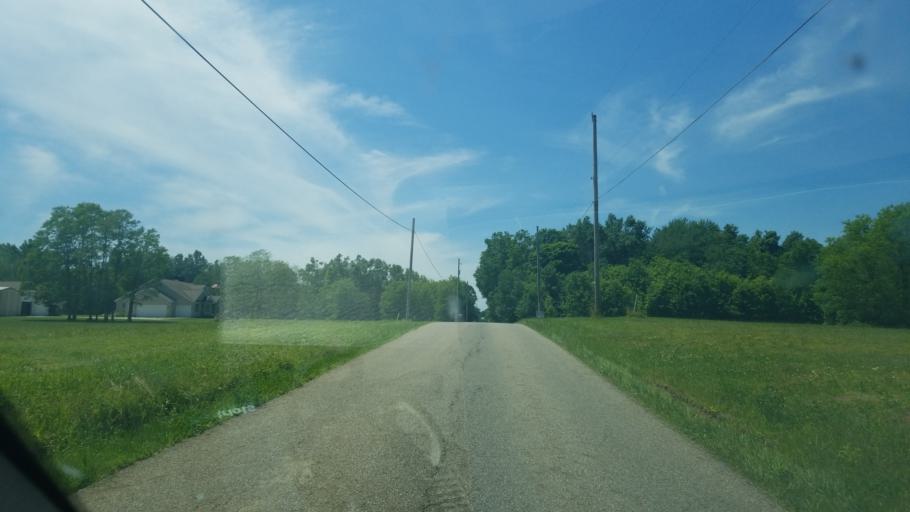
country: US
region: Ohio
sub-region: Stark County
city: Alliance
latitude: 40.8574
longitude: -81.0929
